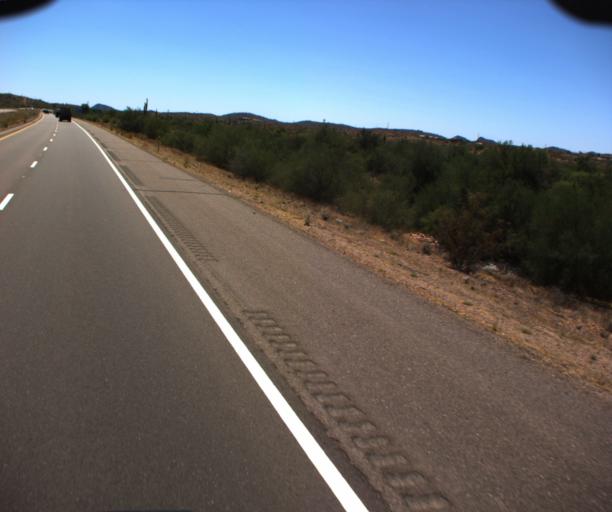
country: US
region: Arizona
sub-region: Maricopa County
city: Fountain Hills
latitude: 33.5737
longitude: -111.6956
